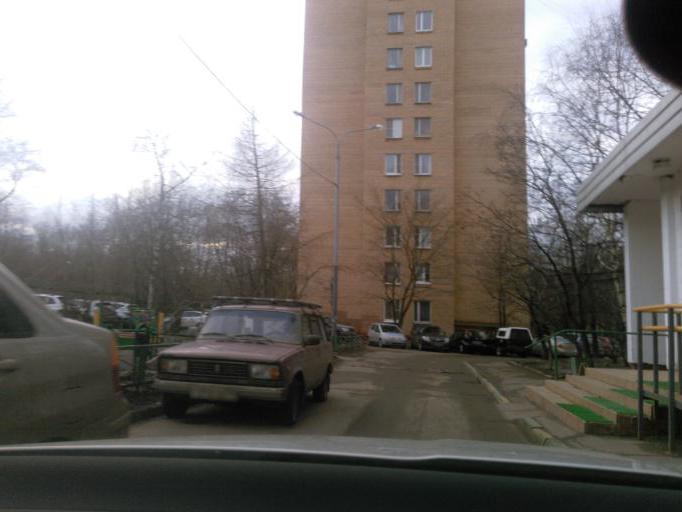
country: RU
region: Moskovskaya
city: Koptevo
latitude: 55.8232
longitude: 37.5307
